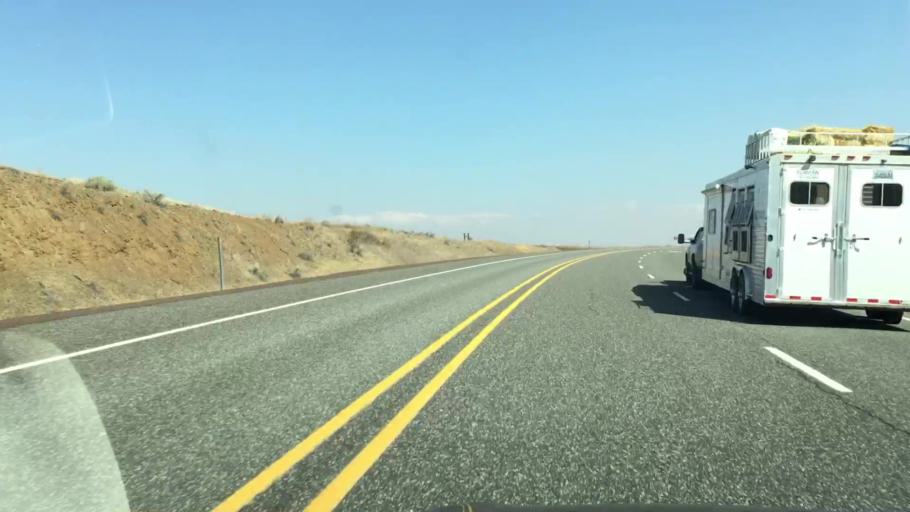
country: US
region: Oregon
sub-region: Wasco County
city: The Dalles
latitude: 45.3230
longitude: -121.1508
